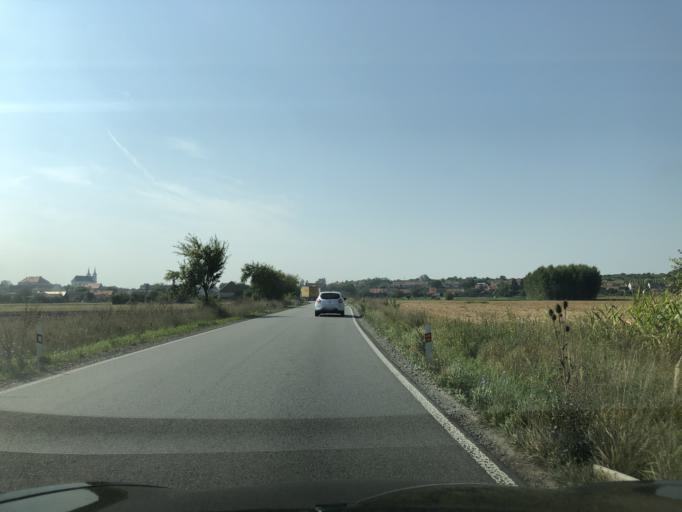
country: CZ
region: South Moravian
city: Drnholec
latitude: 48.8657
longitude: 16.4893
